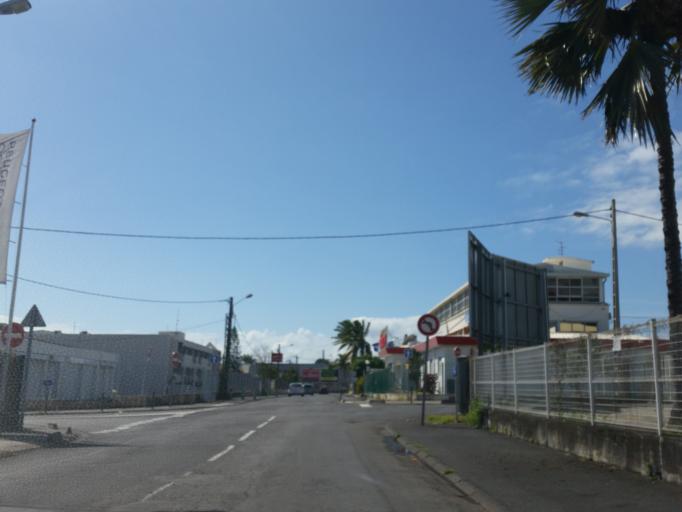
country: RE
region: Reunion
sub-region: Reunion
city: Saint-Denis
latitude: -20.8954
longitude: 55.4960
